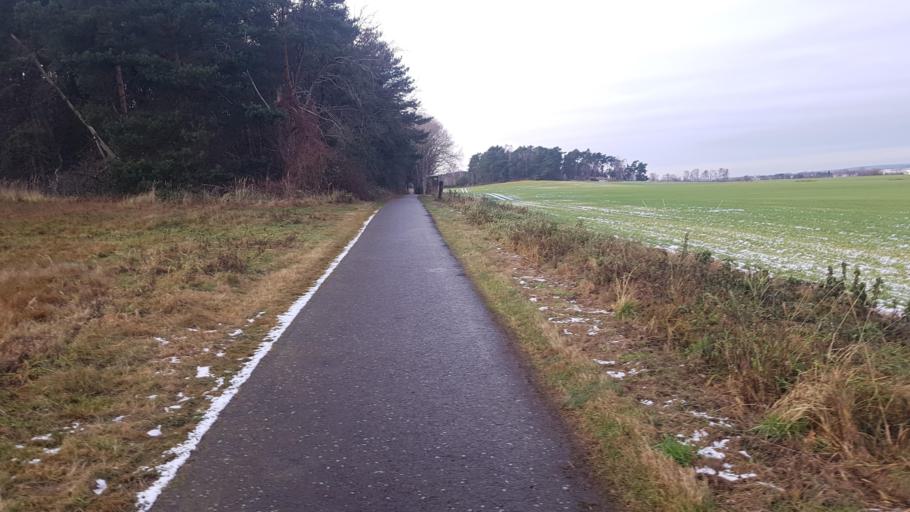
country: DE
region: Brandenburg
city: Hirschfeld
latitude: 51.3922
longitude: 13.5966
